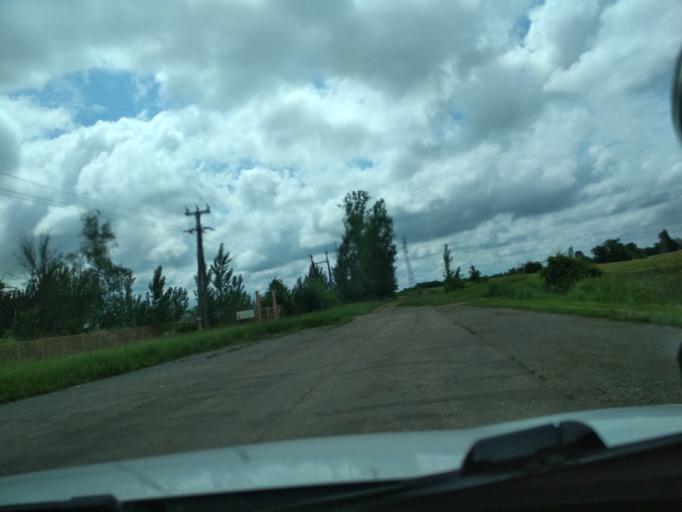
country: HU
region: Jasz-Nagykun-Szolnok
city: Tiszafured
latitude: 47.6061
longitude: 20.7329
